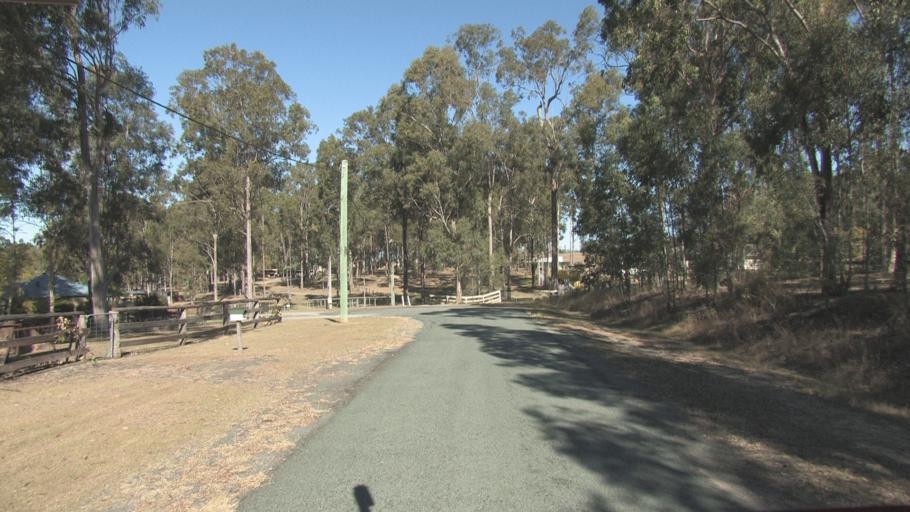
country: AU
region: Queensland
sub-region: Logan
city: North Maclean
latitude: -27.8219
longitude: 152.9814
